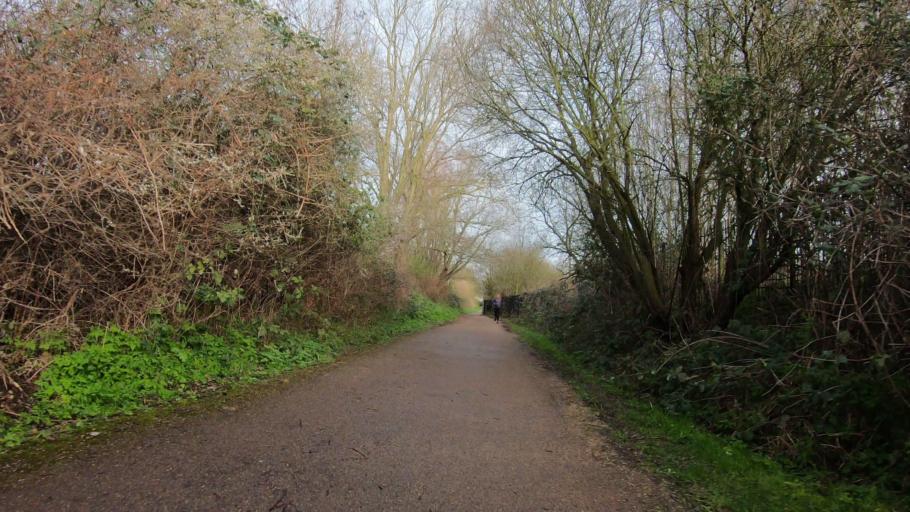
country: GB
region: England
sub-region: Greater London
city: Hackney
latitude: 51.5576
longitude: -0.0246
